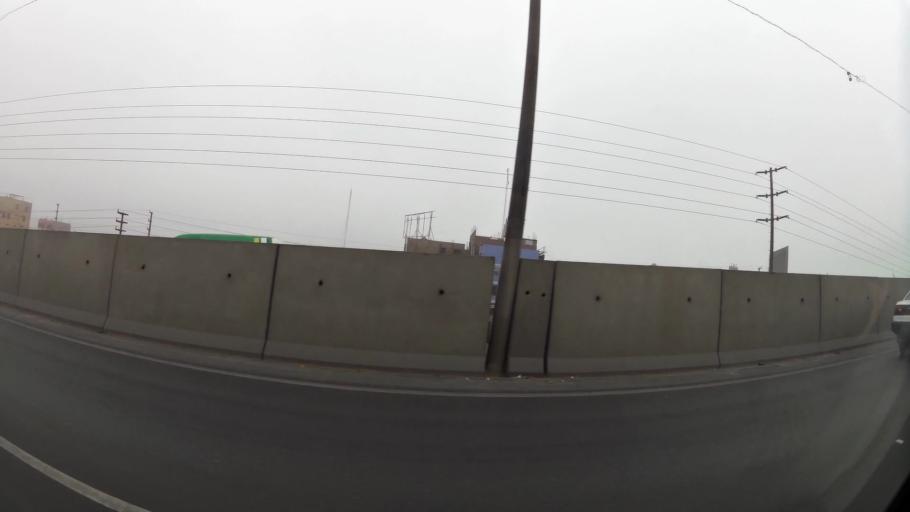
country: PE
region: Lima
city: Ventanilla
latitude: -11.8369
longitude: -77.1091
